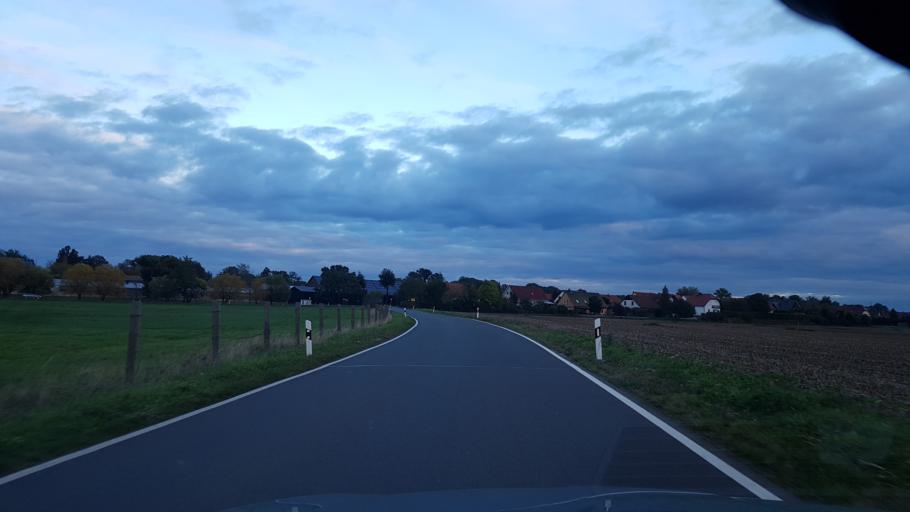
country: DE
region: Saxony
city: Ebersbach
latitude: 51.2790
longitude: 13.6198
